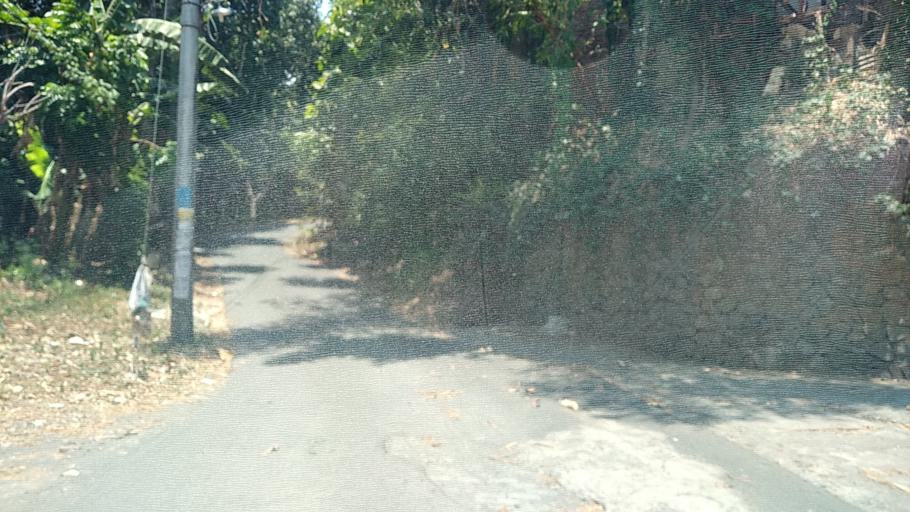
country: ID
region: Central Java
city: Ungaran
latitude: -7.0803
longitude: 110.4232
